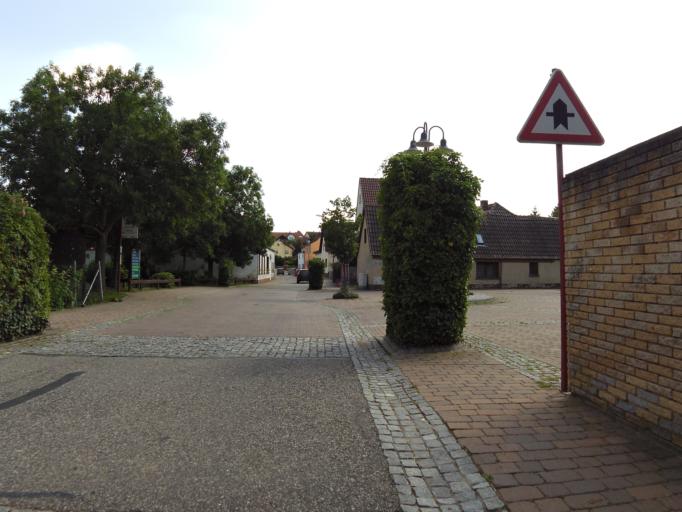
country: DE
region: Rheinland-Pfalz
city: Borrstadt
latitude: 49.5786
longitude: 7.9433
